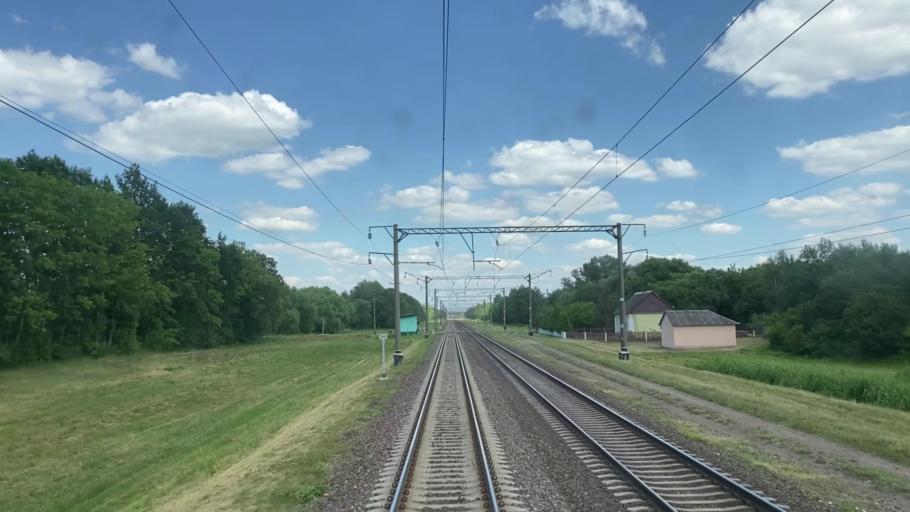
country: BY
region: Brest
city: Charnawchytsy
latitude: 52.1333
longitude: 23.8190
